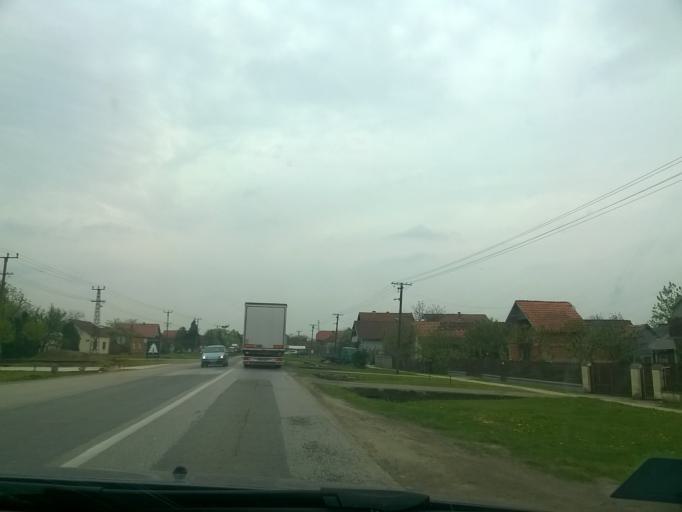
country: RS
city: Hrtkovci
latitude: 44.8900
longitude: 19.7638
